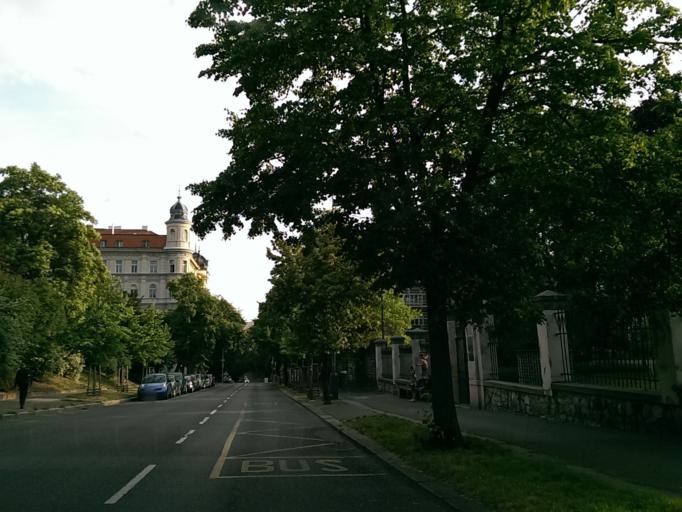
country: CZ
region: Praha
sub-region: Praha 8
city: Karlin
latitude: 50.0802
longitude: 14.4379
